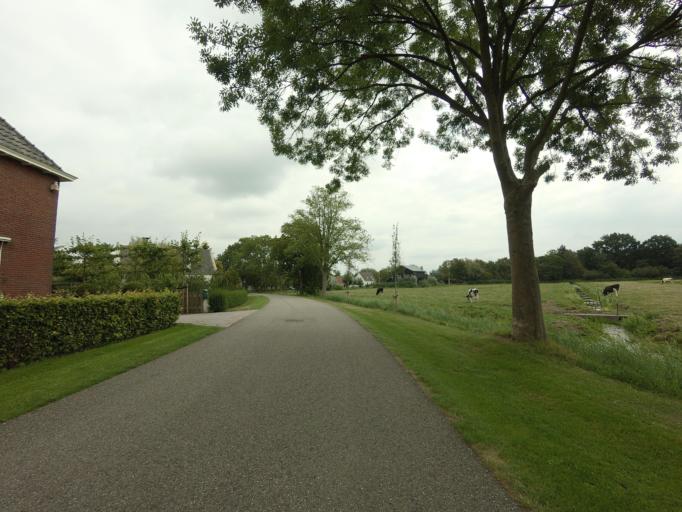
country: NL
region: Utrecht
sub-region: Stichtse Vecht
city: Vreeland
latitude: 52.2287
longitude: 5.0395
